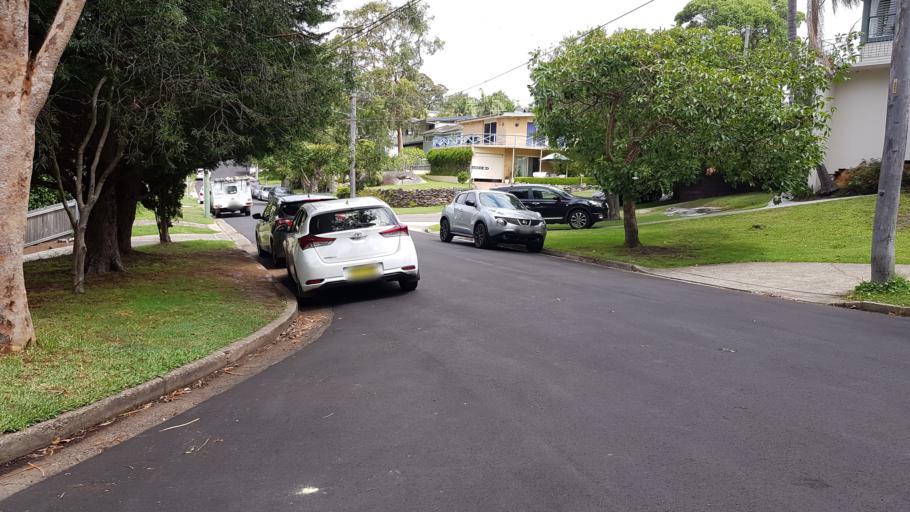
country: AU
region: New South Wales
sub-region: Warringah
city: Narrabeen
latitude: -33.7241
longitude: 151.2786
